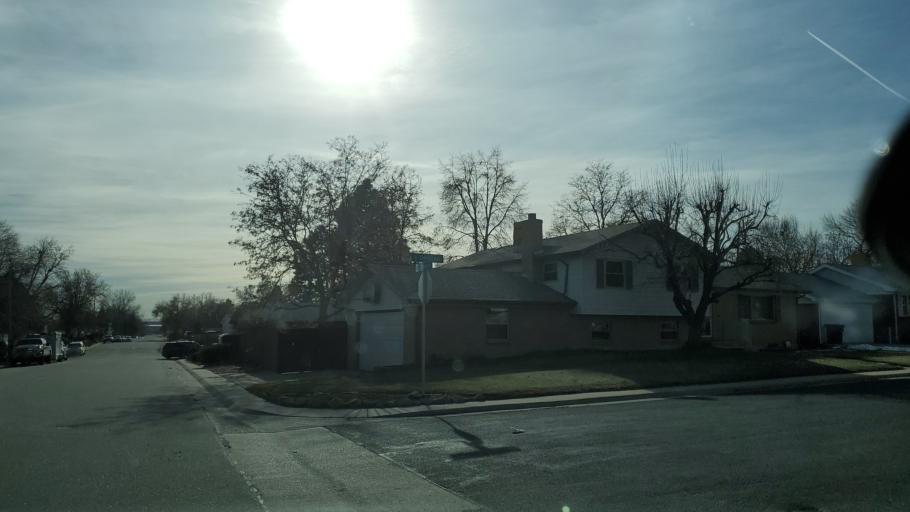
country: US
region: Colorado
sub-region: Adams County
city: Northglenn
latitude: 39.9064
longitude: -104.9605
